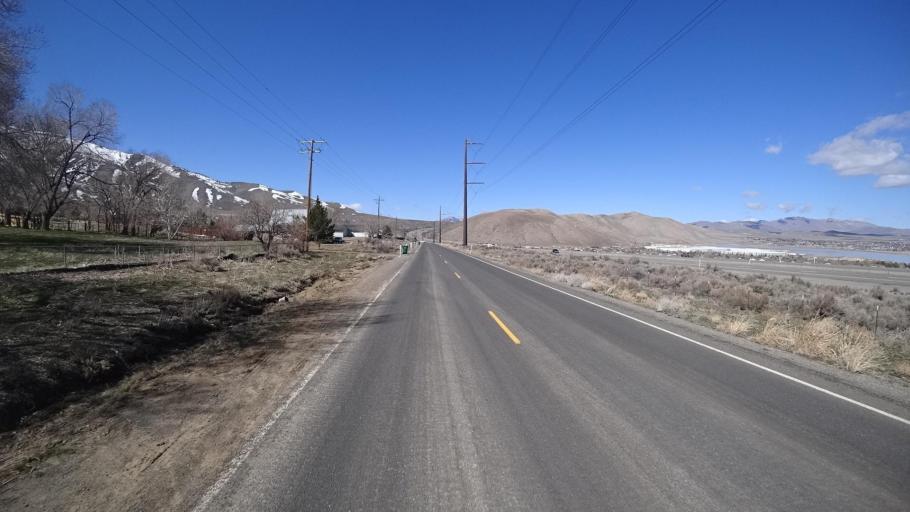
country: US
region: Nevada
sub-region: Washoe County
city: Lemmon Valley
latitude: 39.6253
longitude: -119.9069
